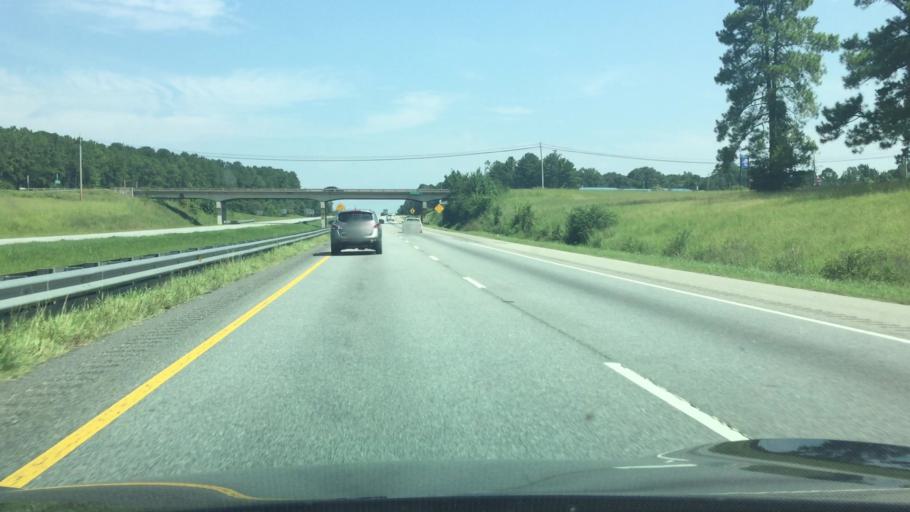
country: US
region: Alabama
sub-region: Shelby County
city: Calera
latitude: 33.1014
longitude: -86.7388
